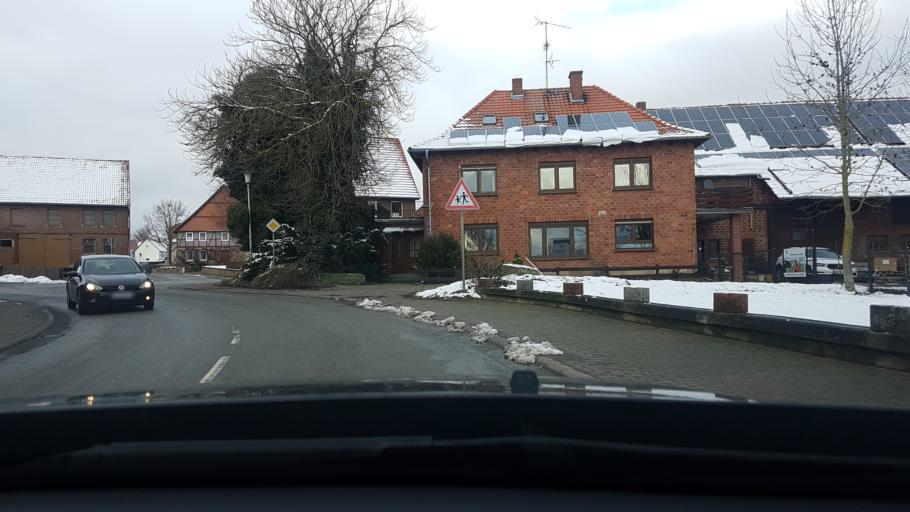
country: DE
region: North Rhine-Westphalia
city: Marsberg
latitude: 51.3857
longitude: 8.8929
